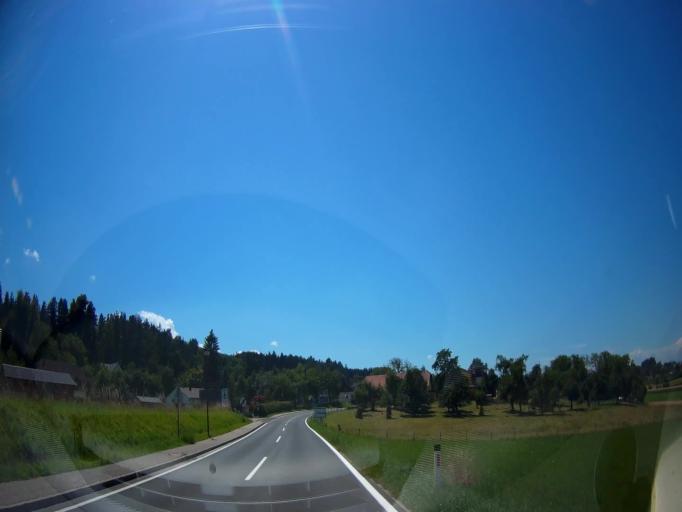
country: AT
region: Carinthia
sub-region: Politischer Bezirk Volkermarkt
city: Eberndorf
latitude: 46.6138
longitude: 14.5860
